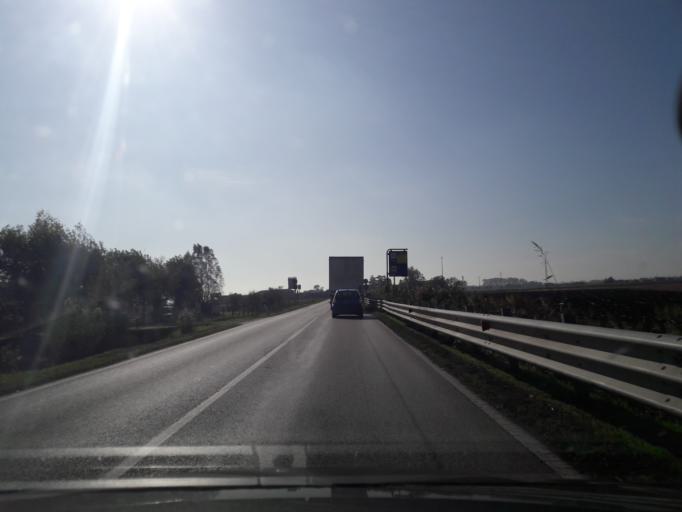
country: IT
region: Veneto
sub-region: Provincia di Rovigo
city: Adria
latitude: 45.0954
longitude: 12.0567
